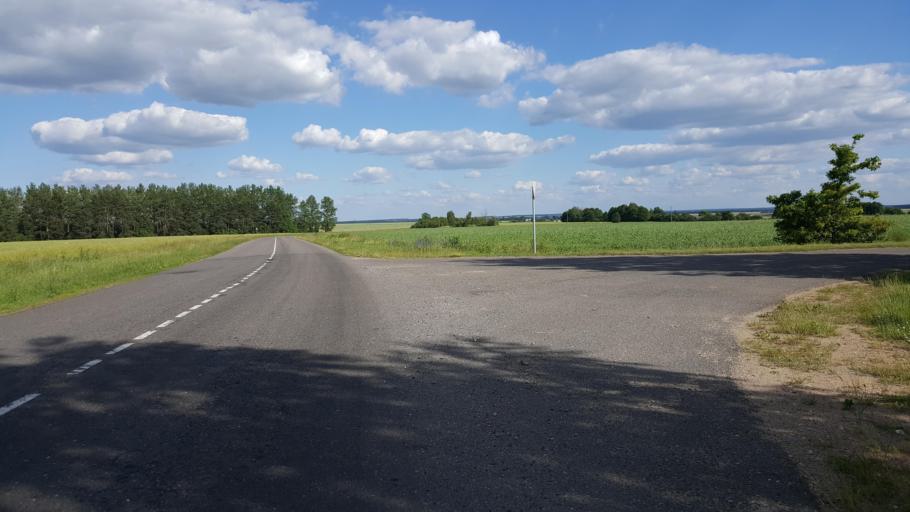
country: BY
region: Brest
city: Kamyanyets
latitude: 52.4468
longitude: 23.7339
